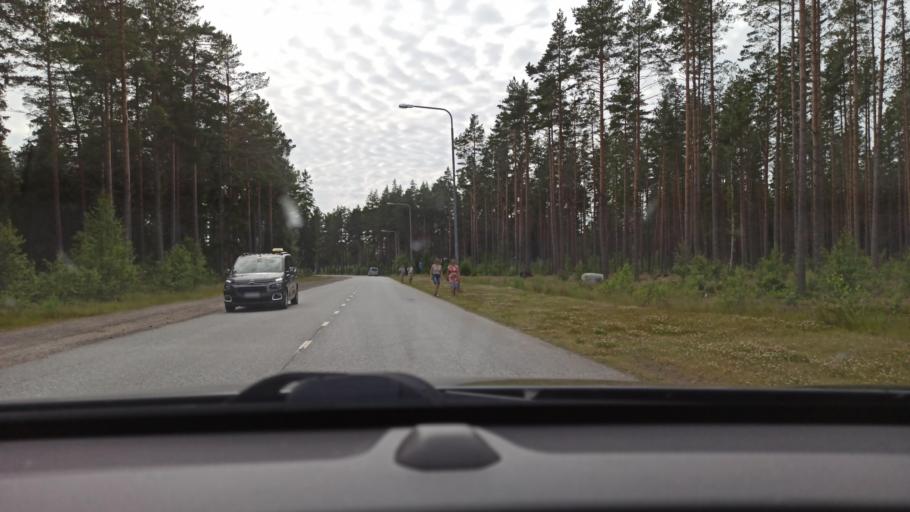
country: FI
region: Satakunta
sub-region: Pori
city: Luvia
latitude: 61.5736
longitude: 21.5219
